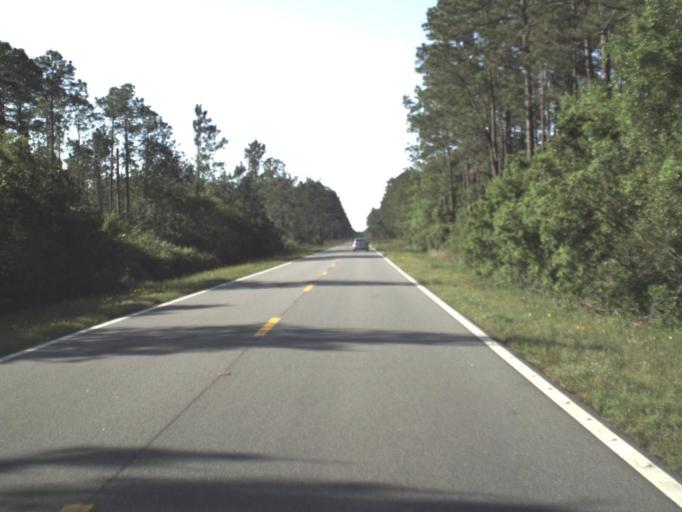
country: US
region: Florida
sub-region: Gulf County
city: Wewahitchka
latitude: 30.1079
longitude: -84.9866
